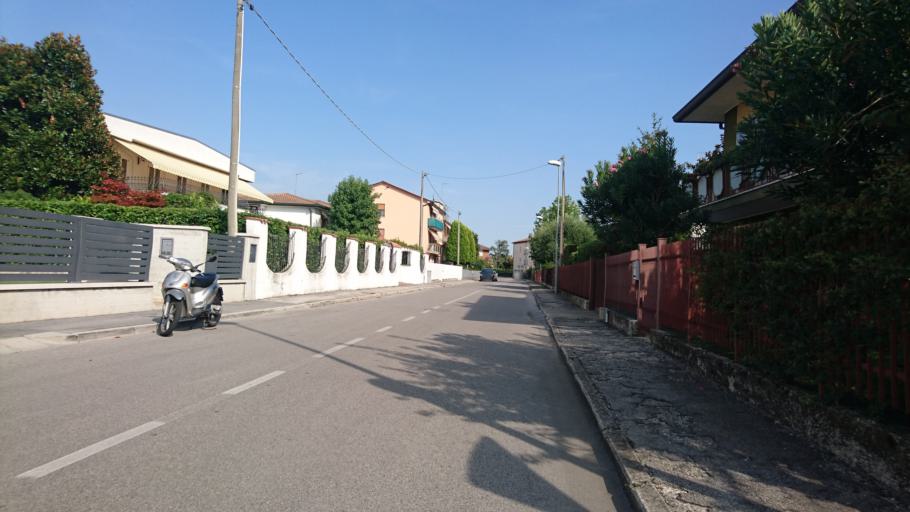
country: IT
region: Veneto
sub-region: Provincia di Padova
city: Tencarola
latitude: 45.3953
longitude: 11.8018
